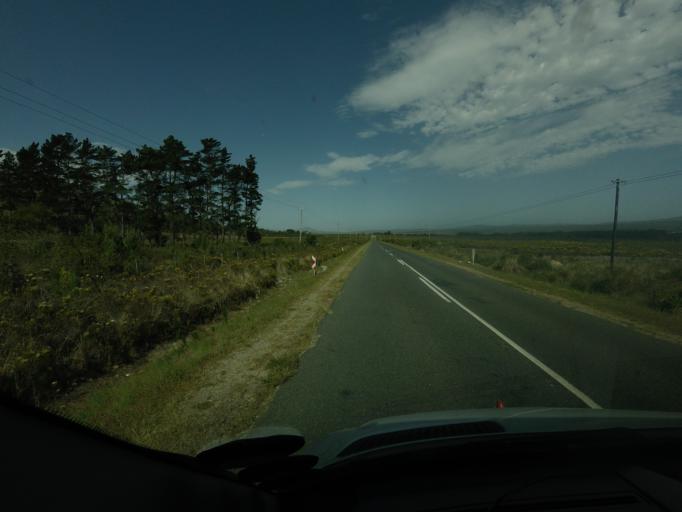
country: ZA
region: Western Cape
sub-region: Overberg District Municipality
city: Caledon
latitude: -34.4194
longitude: 19.4287
